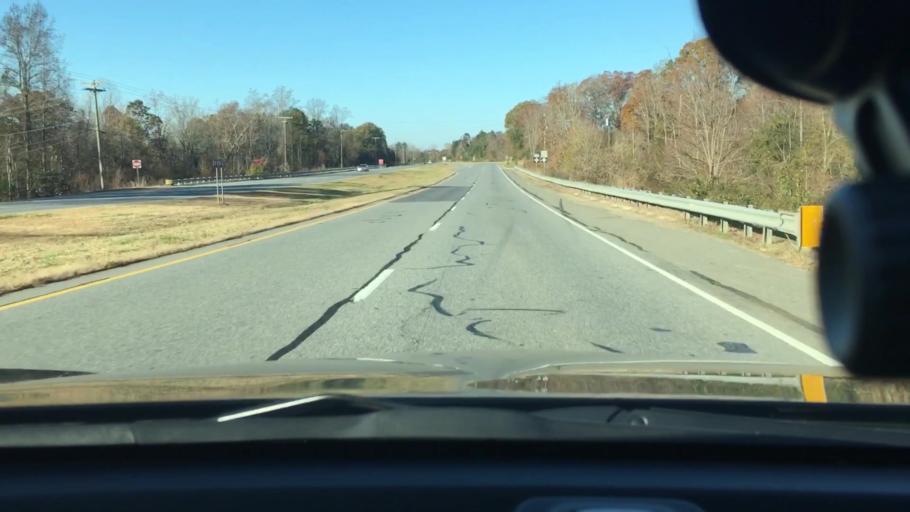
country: US
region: North Carolina
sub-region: Cabarrus County
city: Concord
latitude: 35.3855
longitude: -80.5155
